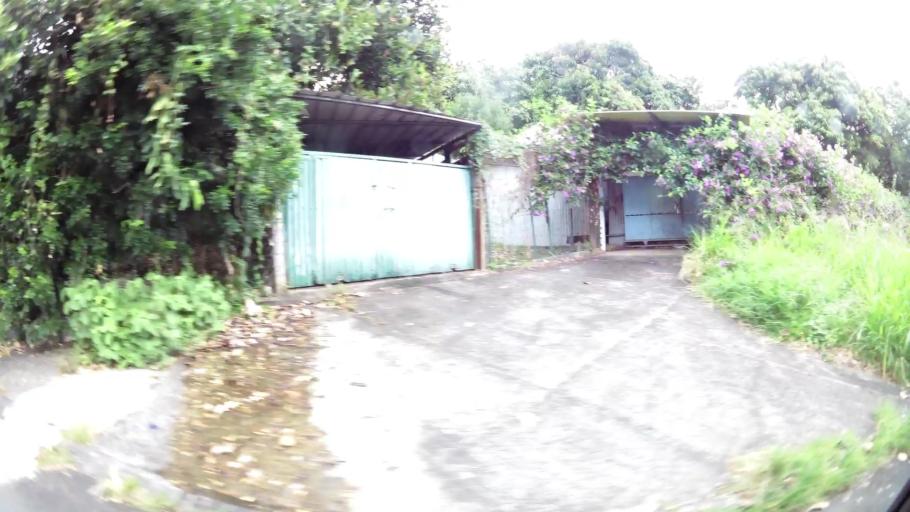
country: RE
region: Reunion
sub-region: Reunion
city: Sainte-Marie
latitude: -20.8993
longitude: 55.5493
